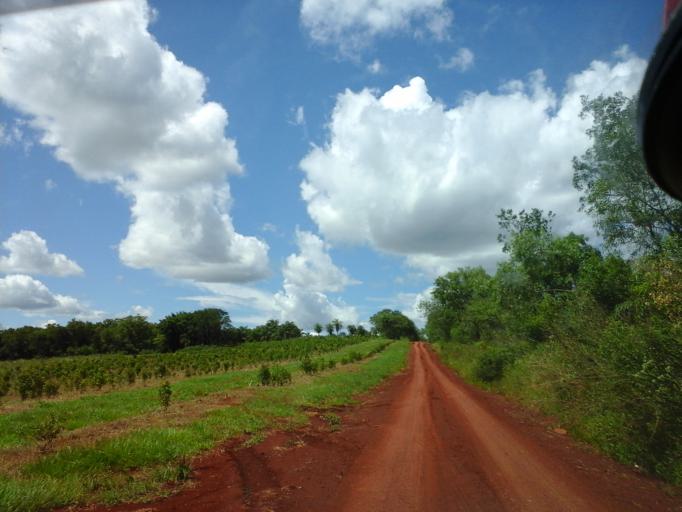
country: AR
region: Misiones
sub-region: Departamento de Apostoles
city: Apostoles
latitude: -27.9806
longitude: -55.7786
